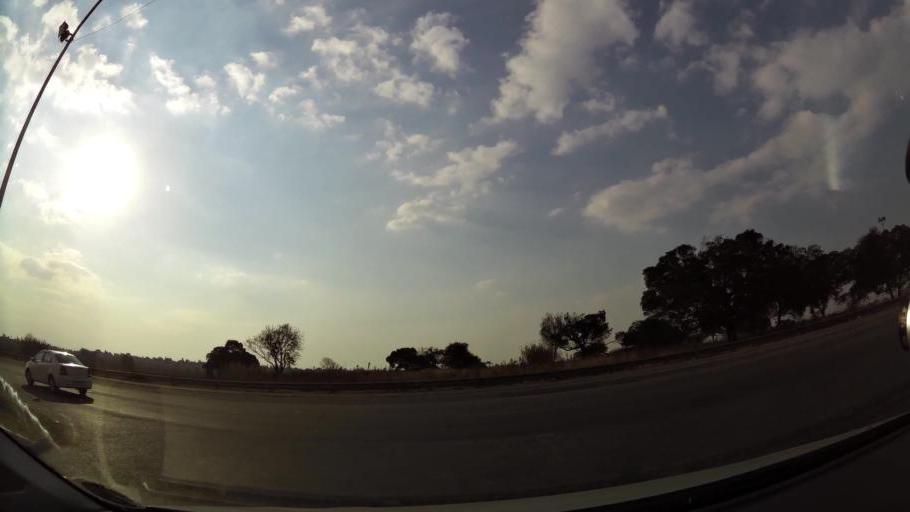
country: ZA
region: Gauteng
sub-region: City of Johannesburg Metropolitan Municipality
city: Modderfontein
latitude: -26.1093
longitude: 28.2049
